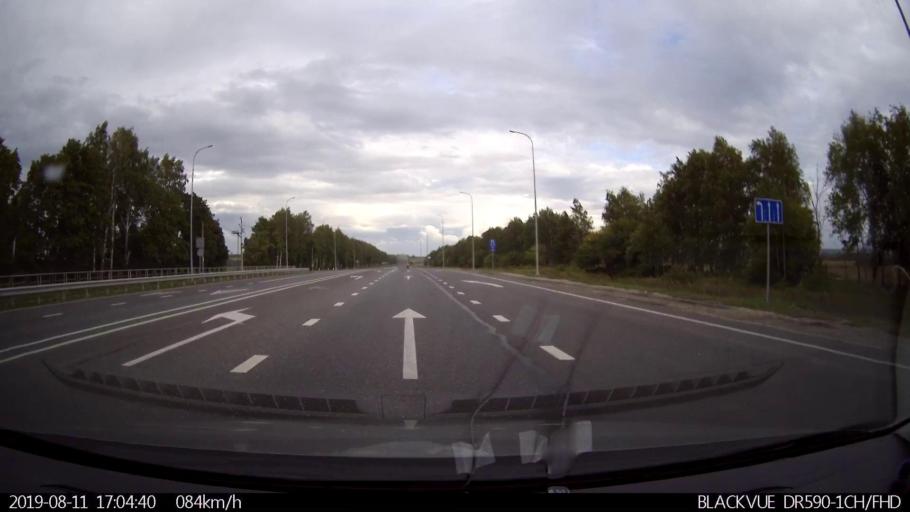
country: RU
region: Ulyanovsk
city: Mayna
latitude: 54.3002
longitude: 47.7689
